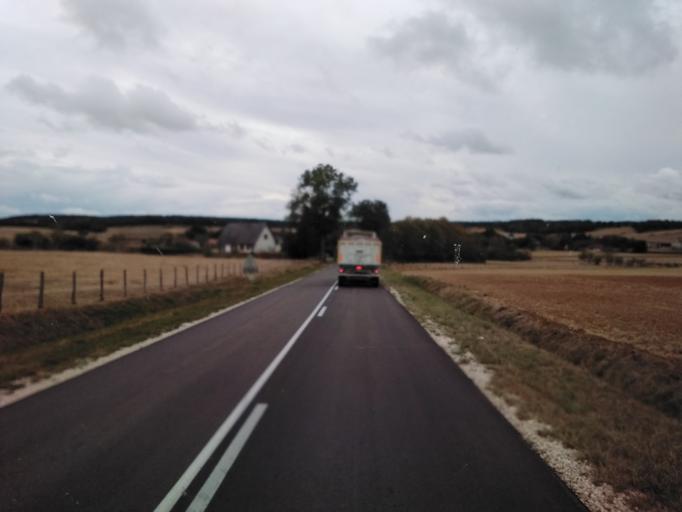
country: FR
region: Champagne-Ardenne
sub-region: Departement de l'Aube
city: Vendeuvre-sur-Barse
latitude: 48.3025
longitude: 4.5189
